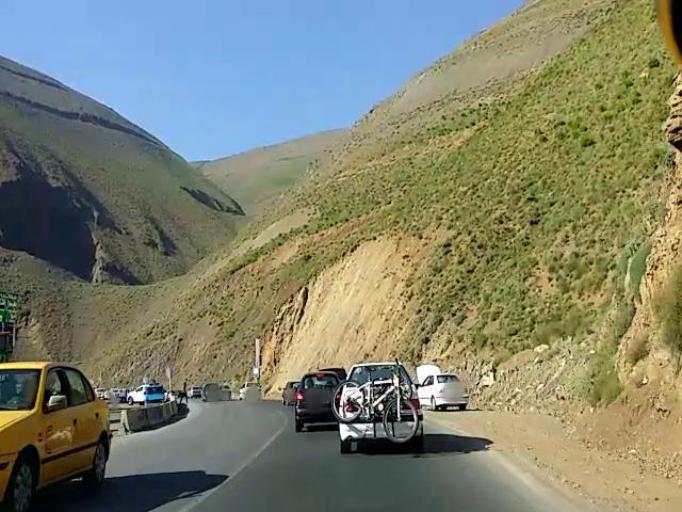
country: IR
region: Tehran
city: Tajrish
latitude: 36.1413
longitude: 51.3074
